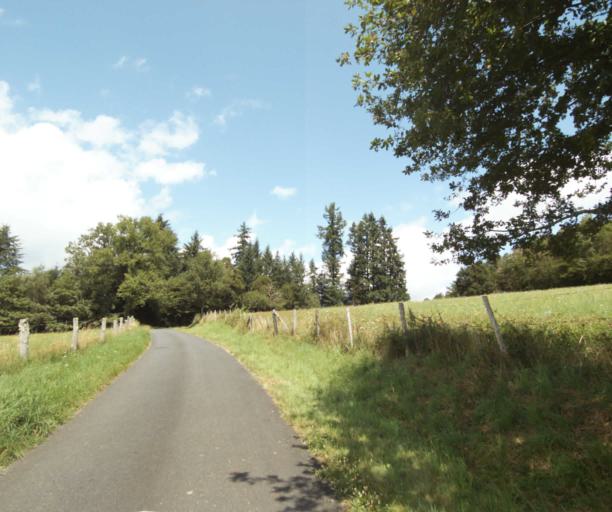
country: FR
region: Limousin
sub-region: Departement de la Correze
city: Sainte-Fortunade
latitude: 45.2036
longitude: 1.8348
